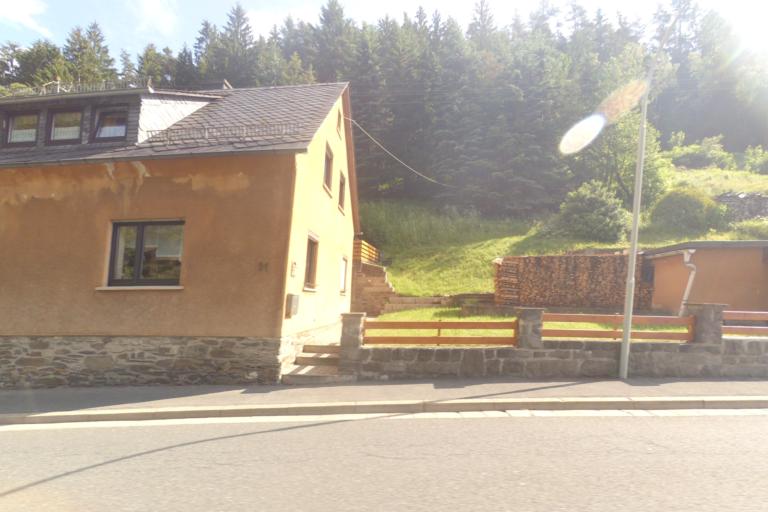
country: DE
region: Bavaria
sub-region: Upper Franconia
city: Ludwigsstadt
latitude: 50.4972
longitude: 11.3733
